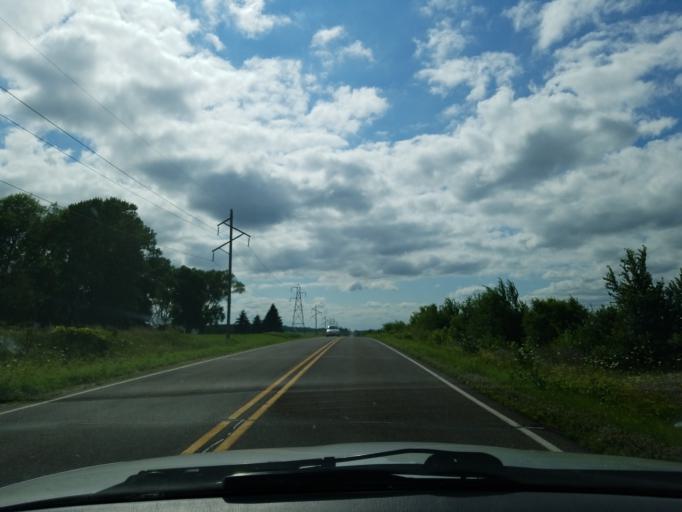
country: US
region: Wisconsin
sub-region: Saint Croix County
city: Roberts
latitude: 45.0356
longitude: -92.5193
